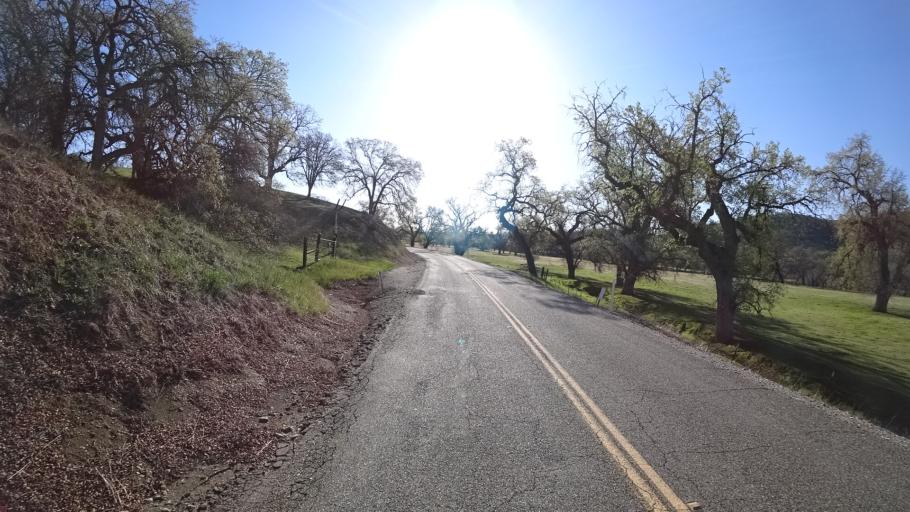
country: US
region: California
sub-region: Tehama County
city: Rancho Tehama Reserve
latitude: 39.7900
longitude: -122.5093
